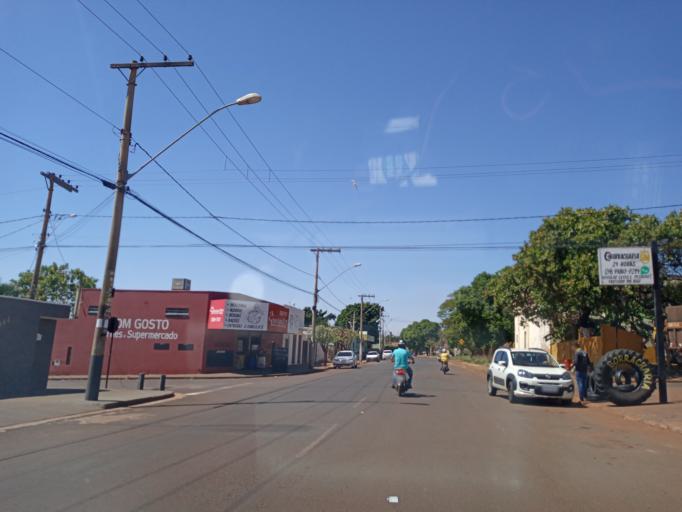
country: BR
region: Minas Gerais
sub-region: Ituiutaba
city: Ituiutaba
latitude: -18.9580
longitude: -49.4583
